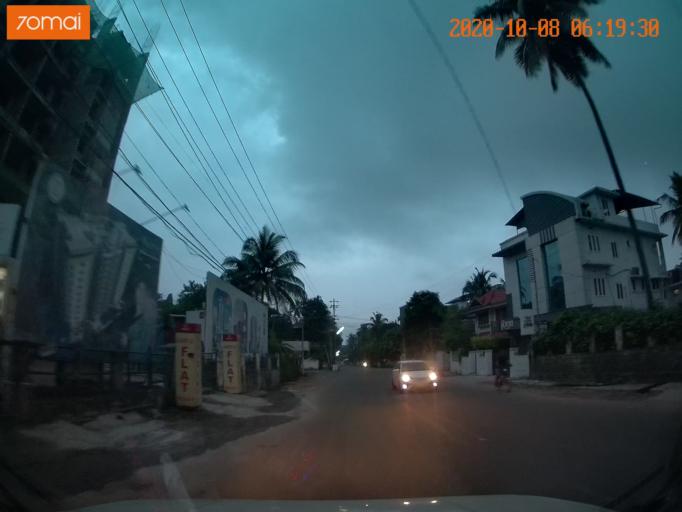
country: IN
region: Kerala
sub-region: Thrissur District
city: Trichur
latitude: 10.5164
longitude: 76.2369
